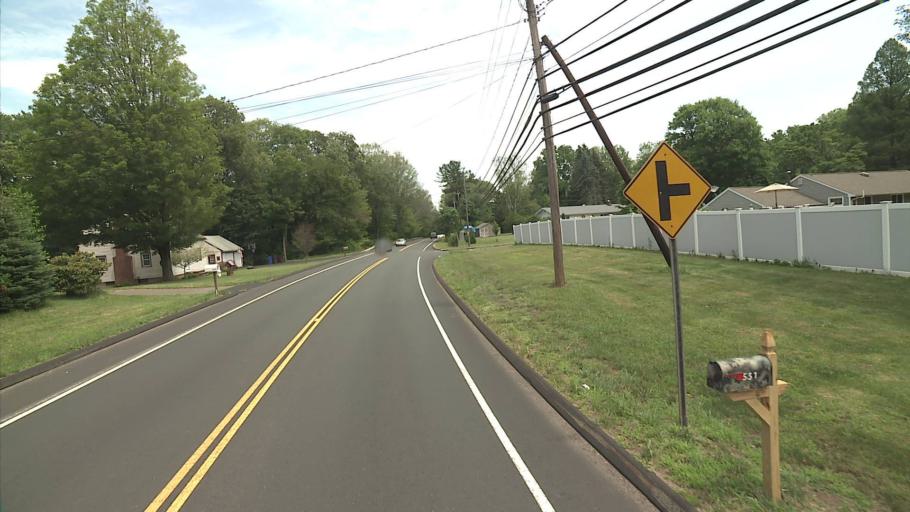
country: US
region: Connecticut
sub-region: New Haven County
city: North Branford
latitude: 41.3696
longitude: -72.7957
